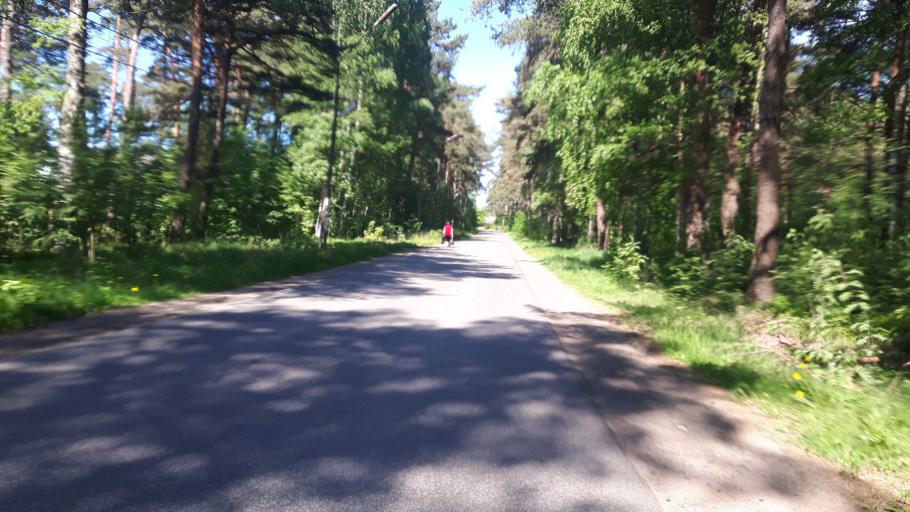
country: RU
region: Leningrad
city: Lebyazh'ye
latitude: 59.9647
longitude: 29.4078
